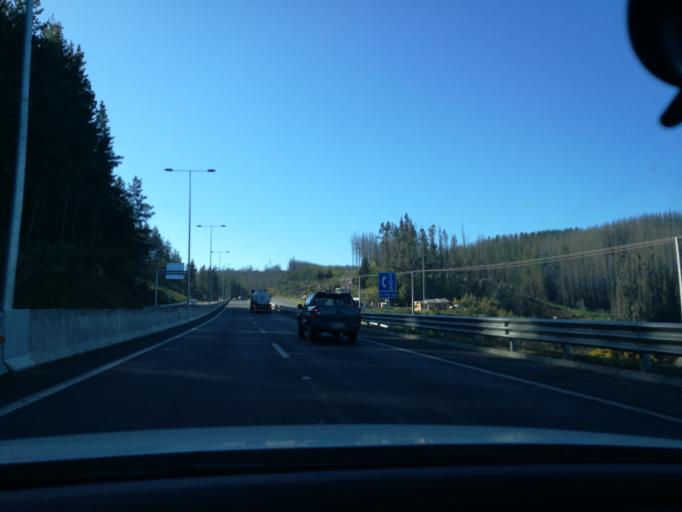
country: CL
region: Biobio
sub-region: Provincia de Concepcion
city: Penco
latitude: -36.8568
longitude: -72.8679
